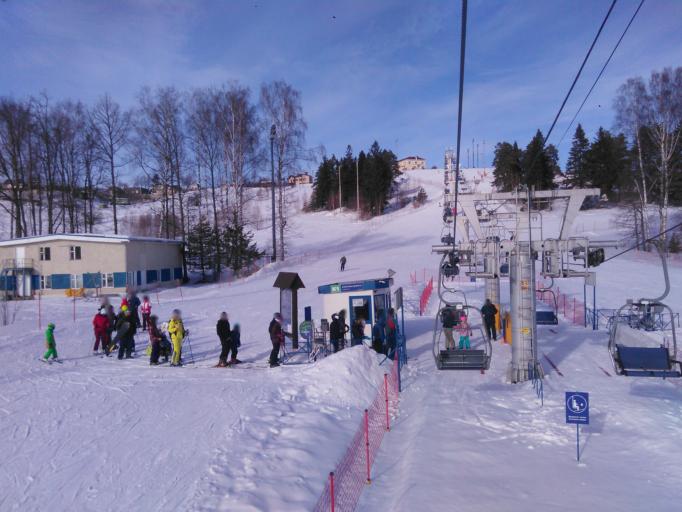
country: RU
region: Moskovskaya
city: Dedenevo
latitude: 56.2696
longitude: 37.5610
